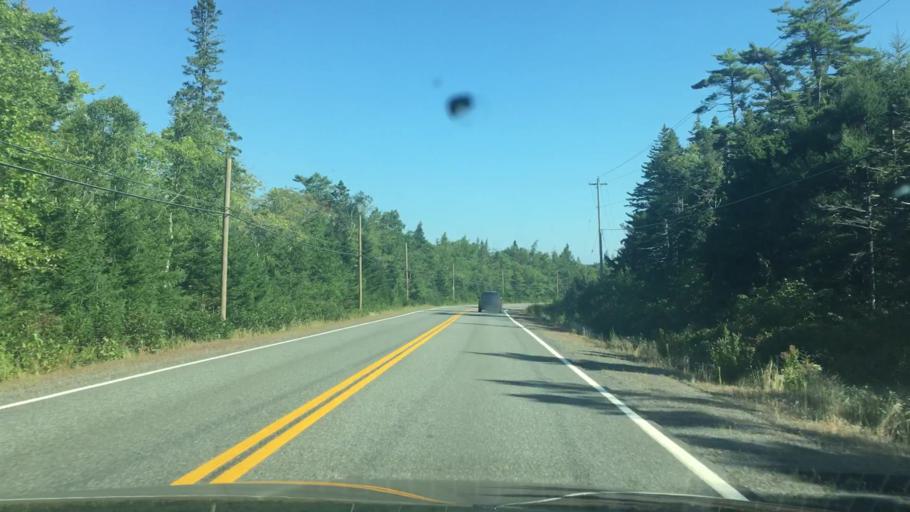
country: CA
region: Nova Scotia
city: Cole Harbour
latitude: 44.7949
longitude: -62.8889
